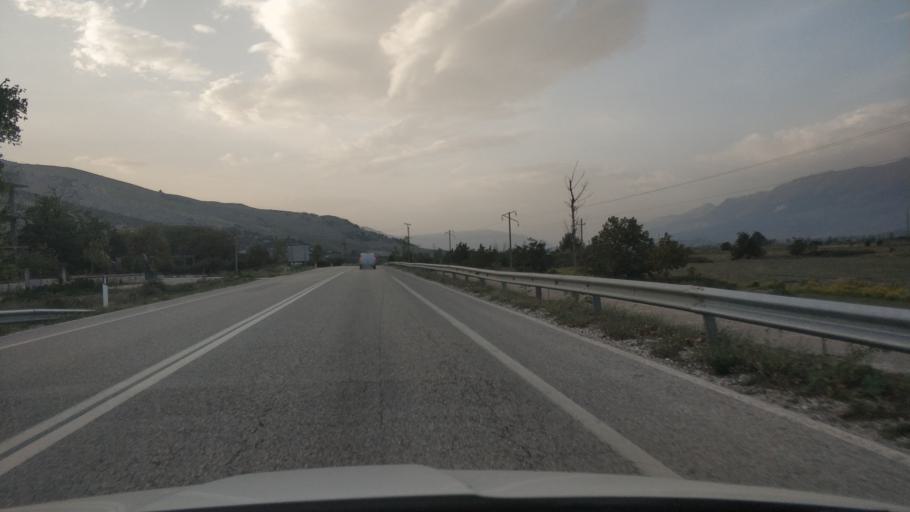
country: AL
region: Gjirokaster
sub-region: Rrethi i Gjirokastres
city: Libohove
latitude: 39.9545
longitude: 20.2515
